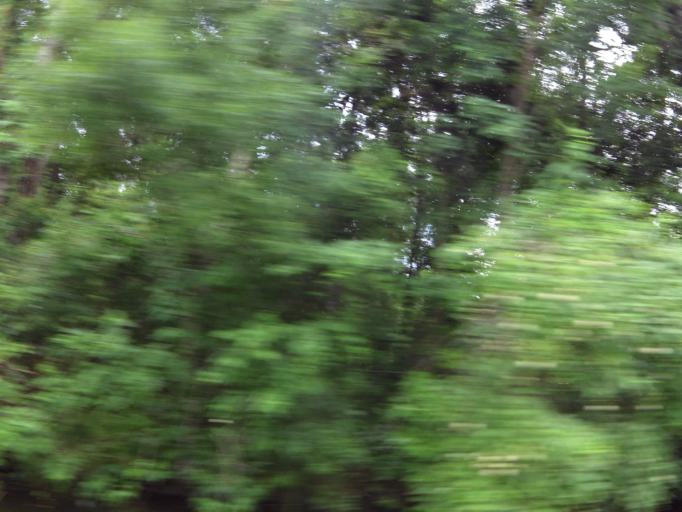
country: US
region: Florida
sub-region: Nassau County
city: Nassau Village-Ratliff
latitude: 30.5509
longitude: -81.7033
